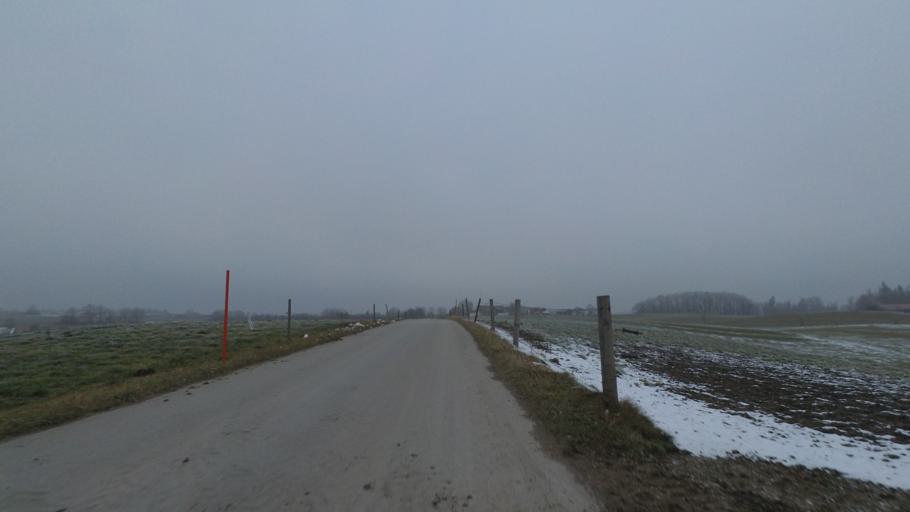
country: DE
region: Bavaria
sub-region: Upper Bavaria
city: Chieming
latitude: 47.8868
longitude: 12.5596
